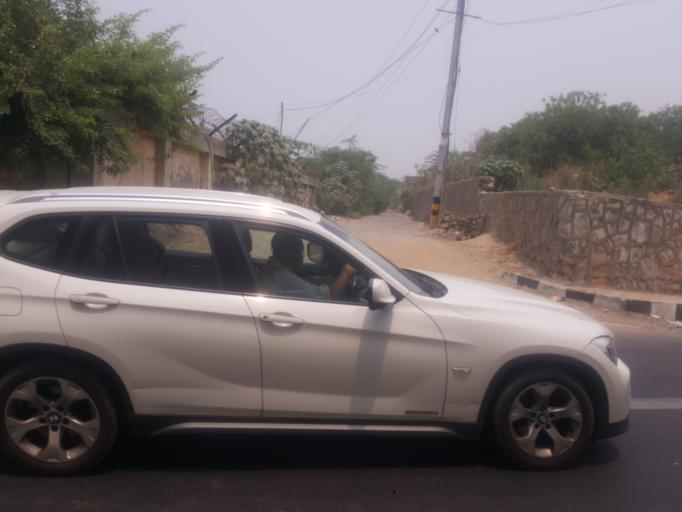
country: IN
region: NCT
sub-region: Central Delhi
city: Karol Bagh
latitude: 28.5400
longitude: 77.1318
